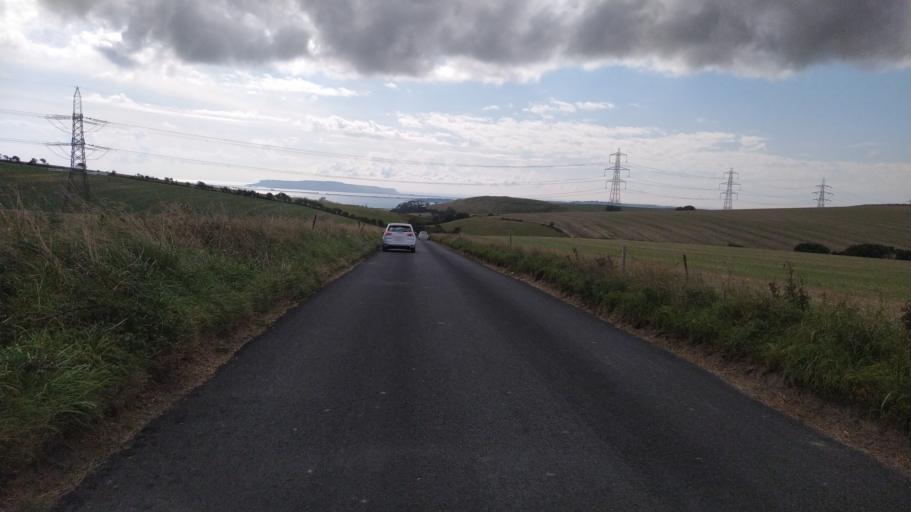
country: GB
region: England
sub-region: Dorset
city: Overcombe
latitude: 50.6642
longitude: -2.4279
